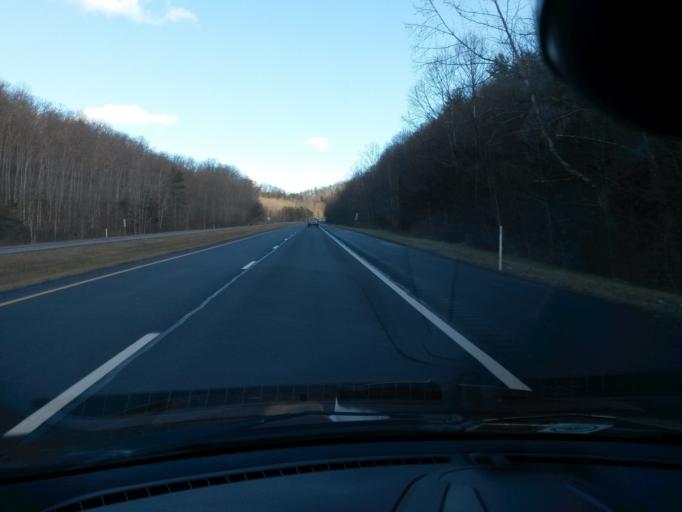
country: US
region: West Virginia
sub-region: Mercer County
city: Athens
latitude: 37.3450
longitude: -80.9494
